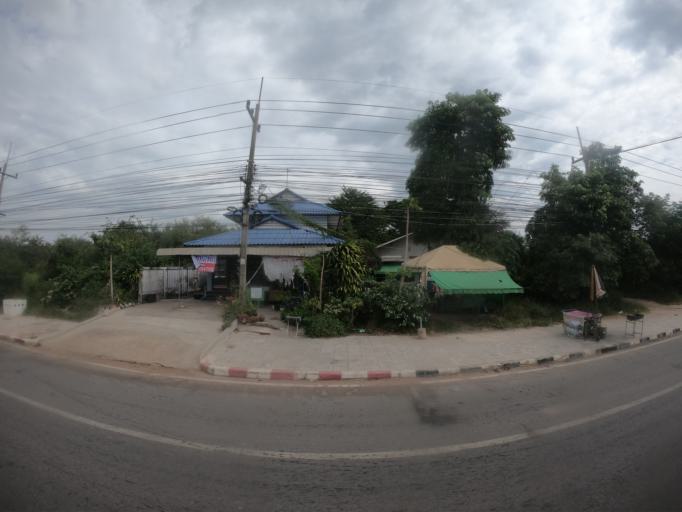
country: TH
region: Maha Sarakham
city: Maha Sarakham
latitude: 16.2243
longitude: 103.2721
